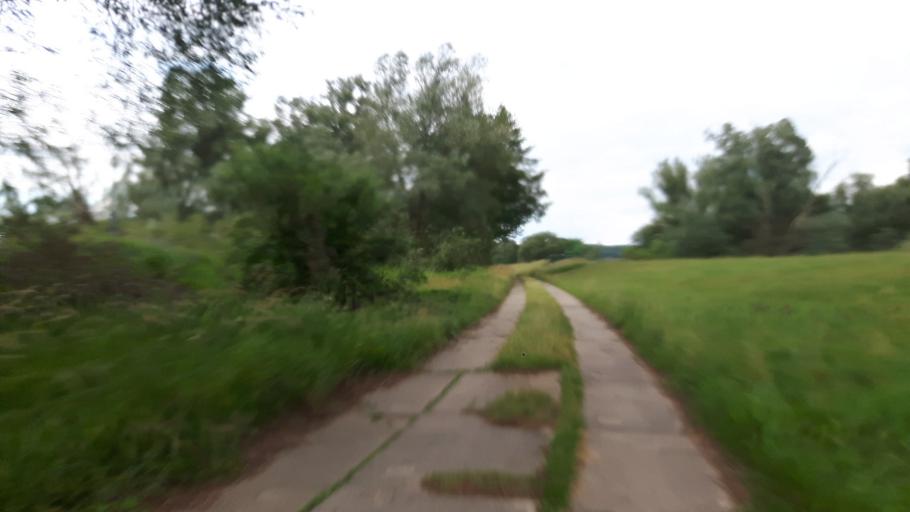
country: PL
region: West Pomeranian Voivodeship
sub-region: Powiat gryfinski
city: Widuchowa
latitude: 53.0808
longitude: 14.3541
